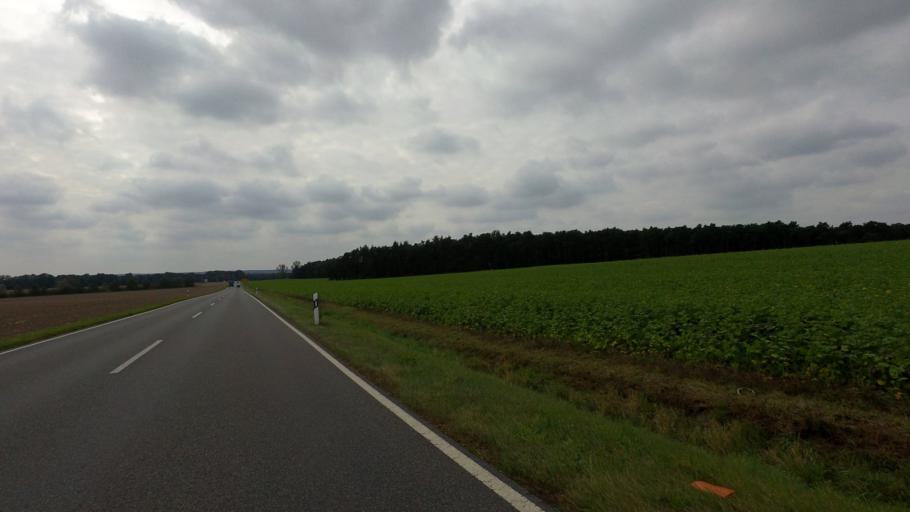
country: DE
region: Brandenburg
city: Luckau
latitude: 51.8212
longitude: 13.6810
